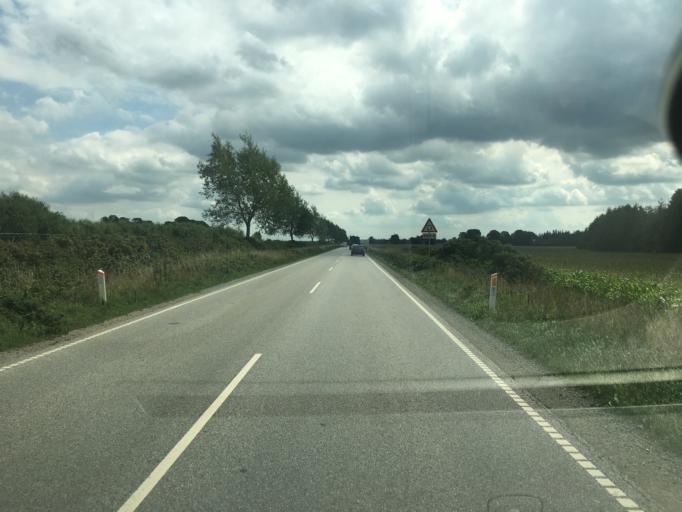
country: DK
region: South Denmark
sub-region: Aabenraa Kommune
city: Tinglev
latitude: 54.9736
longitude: 9.3059
